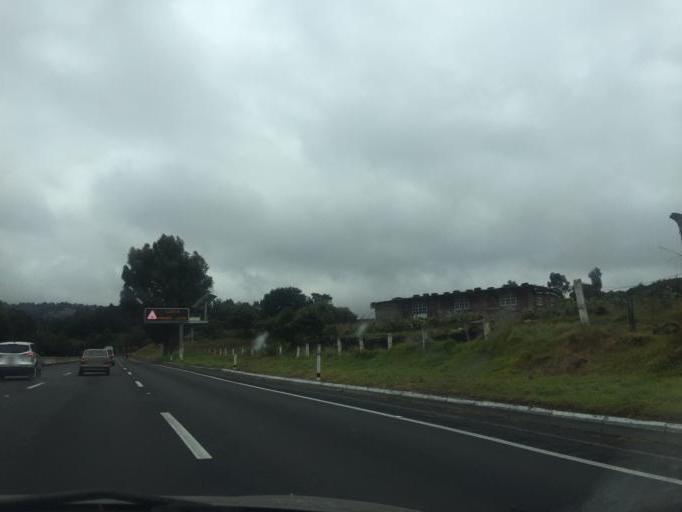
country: MX
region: Mexico City
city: Xochimilco
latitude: 19.1949
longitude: -99.1549
